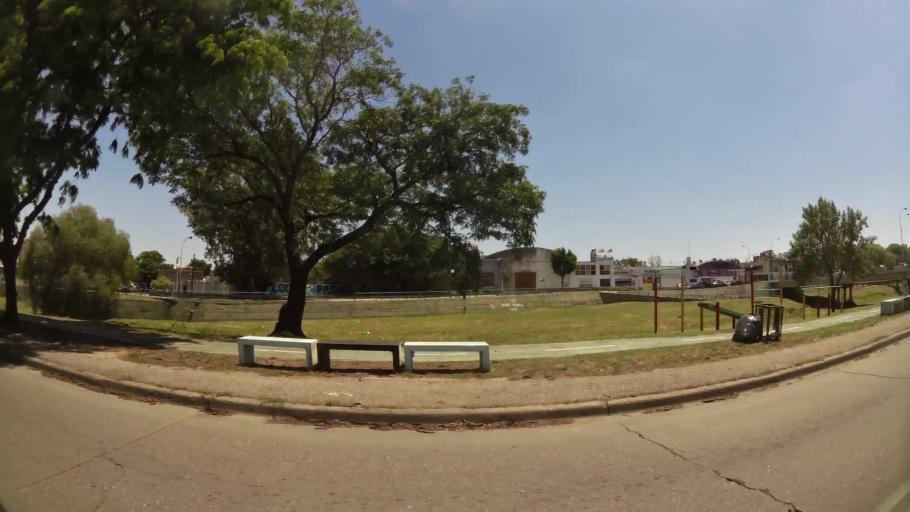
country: AR
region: Cordoba
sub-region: Departamento de Capital
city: Cordoba
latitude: -31.3975
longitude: -64.2030
